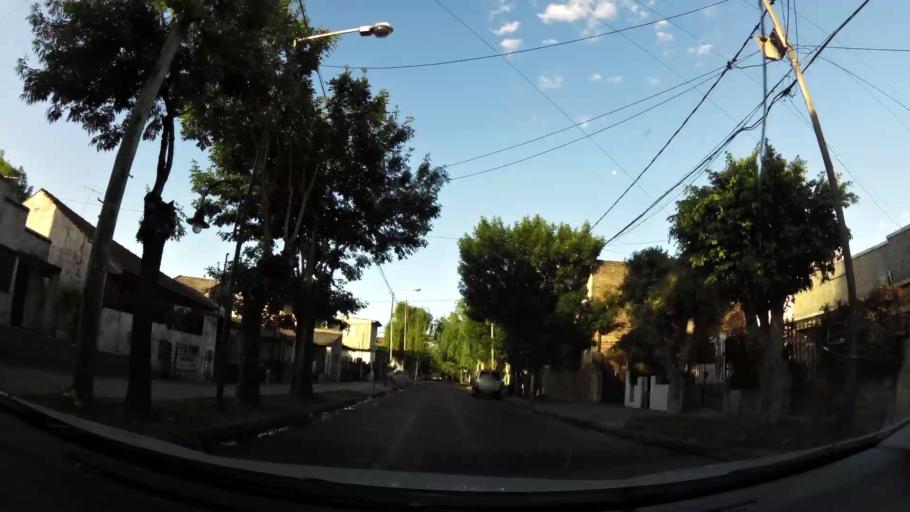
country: AR
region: Buenos Aires
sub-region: Partido de Tigre
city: Tigre
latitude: -34.4433
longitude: -58.5692
